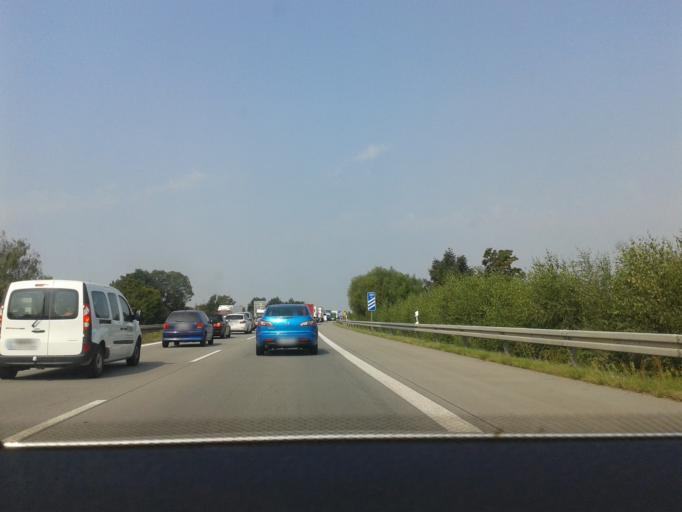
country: DE
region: Saxony
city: Grimma
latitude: 51.2579
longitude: 12.7189
